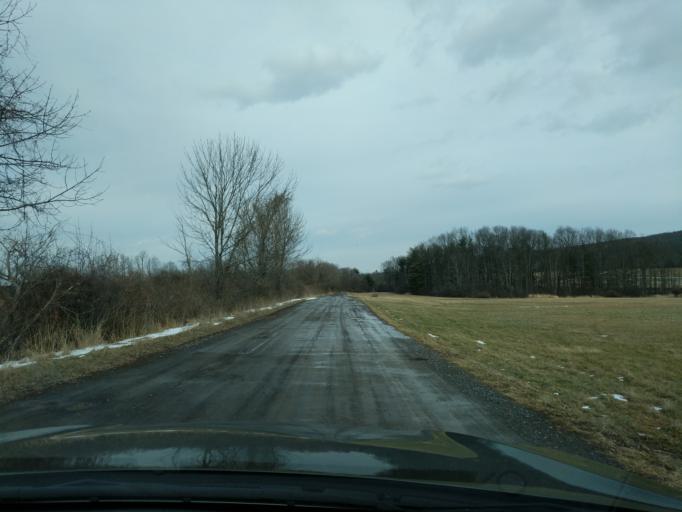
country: US
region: New York
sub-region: Tompkins County
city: Northeast Ithaca
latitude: 42.4457
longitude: -76.4418
